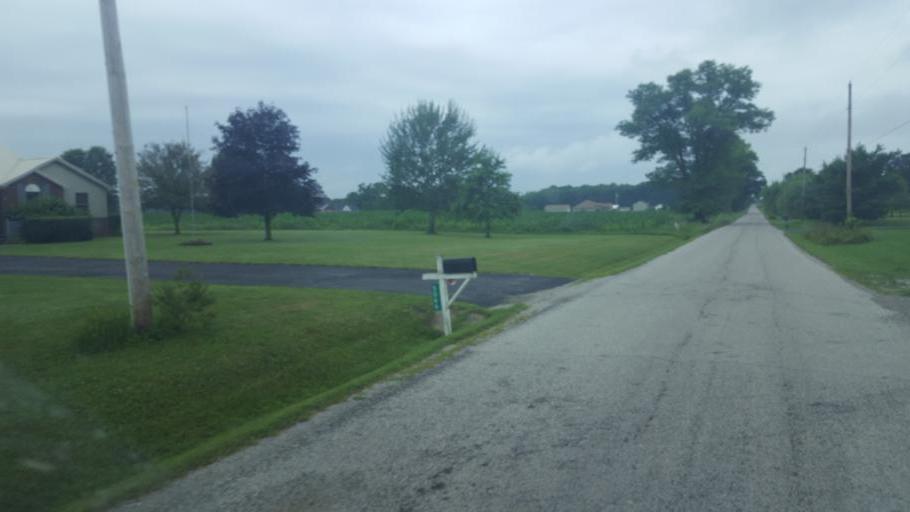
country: US
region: Ohio
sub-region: Knox County
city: Centerburg
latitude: 40.3814
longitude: -82.7780
